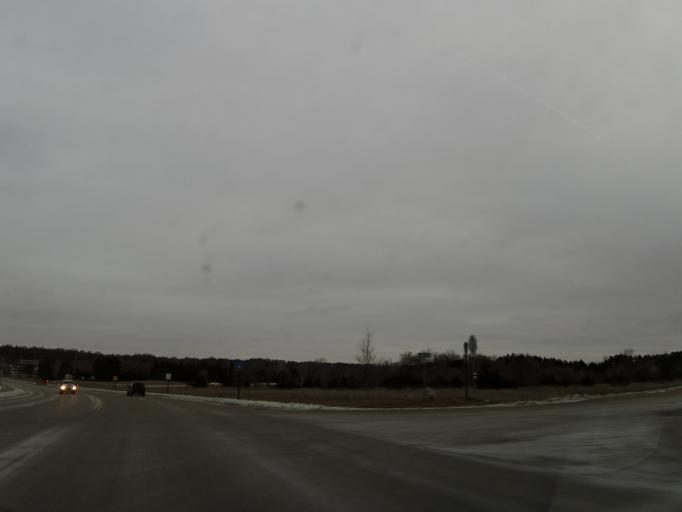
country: US
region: Minnesota
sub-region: Scott County
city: Jordan
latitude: 44.6744
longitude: -93.6416
